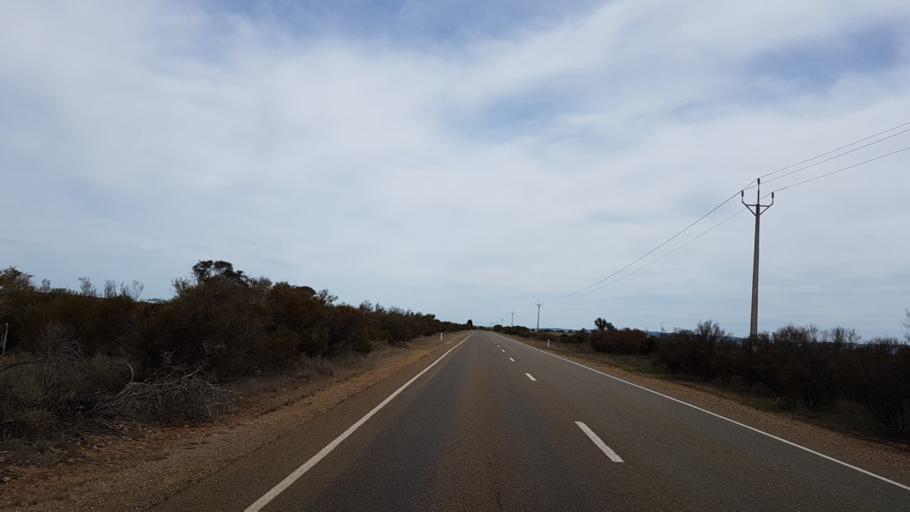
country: AU
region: South Australia
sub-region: Peterborough
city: Peterborough
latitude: -32.9870
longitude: 138.7998
